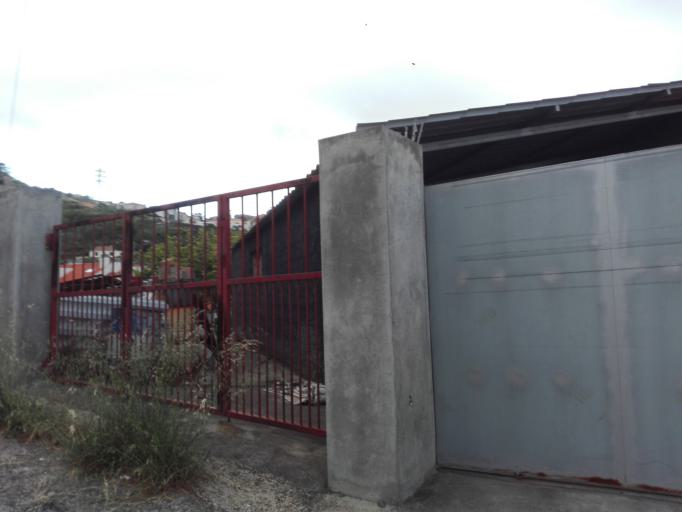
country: PT
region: Madeira
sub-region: Santa Cruz
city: Camacha
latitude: 32.6574
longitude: -16.8282
